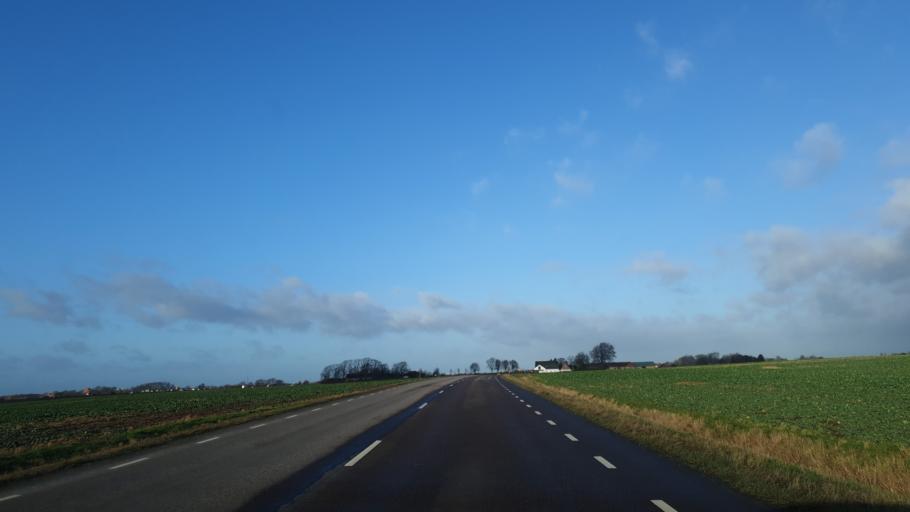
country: SE
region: Skane
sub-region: Vellinge Kommun
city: Vellinge
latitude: 55.4825
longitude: 13.0258
